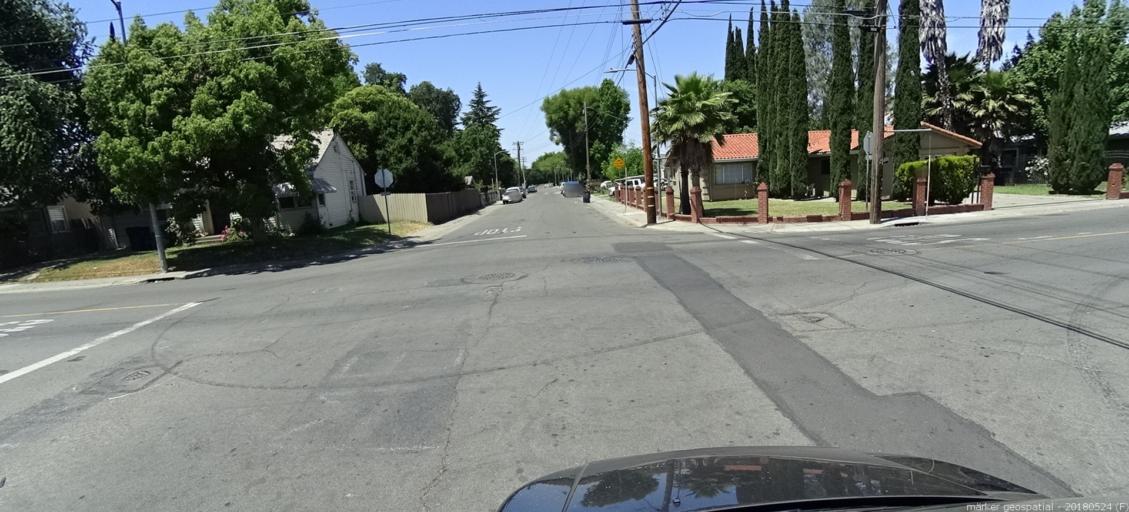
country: US
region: California
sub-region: Sacramento County
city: Sacramento
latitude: 38.6169
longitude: -121.4592
